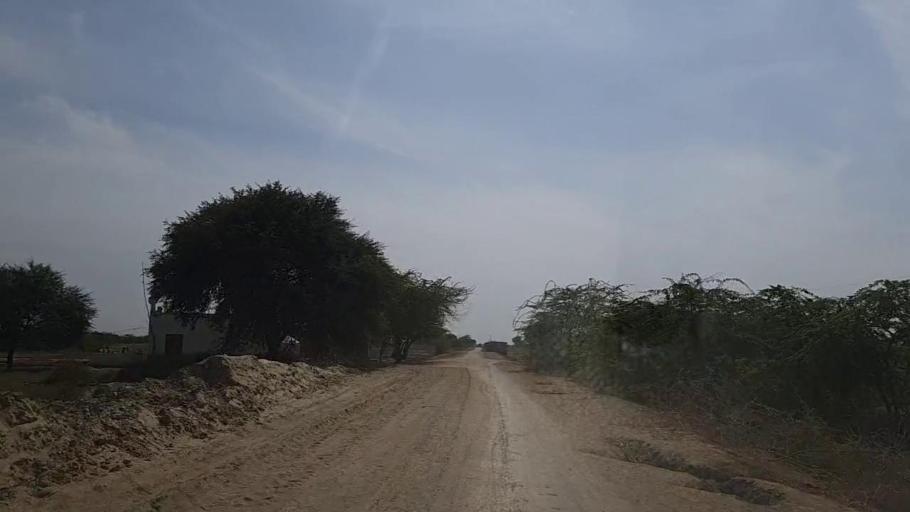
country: PK
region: Sindh
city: Kunri
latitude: 25.1846
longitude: 69.4592
